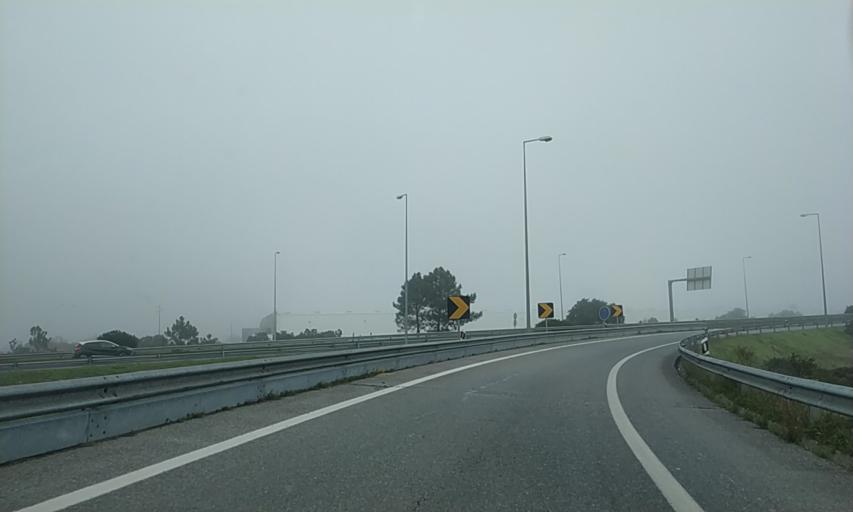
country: PT
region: Setubal
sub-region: Montijo
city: Montijo
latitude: 38.6795
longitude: -8.9435
